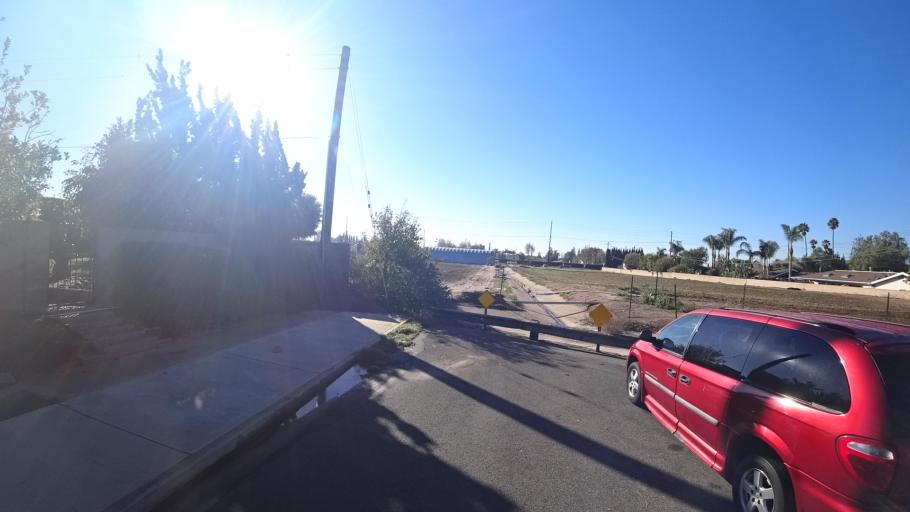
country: US
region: California
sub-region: Orange County
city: North Tustin
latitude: 33.7606
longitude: -117.8027
